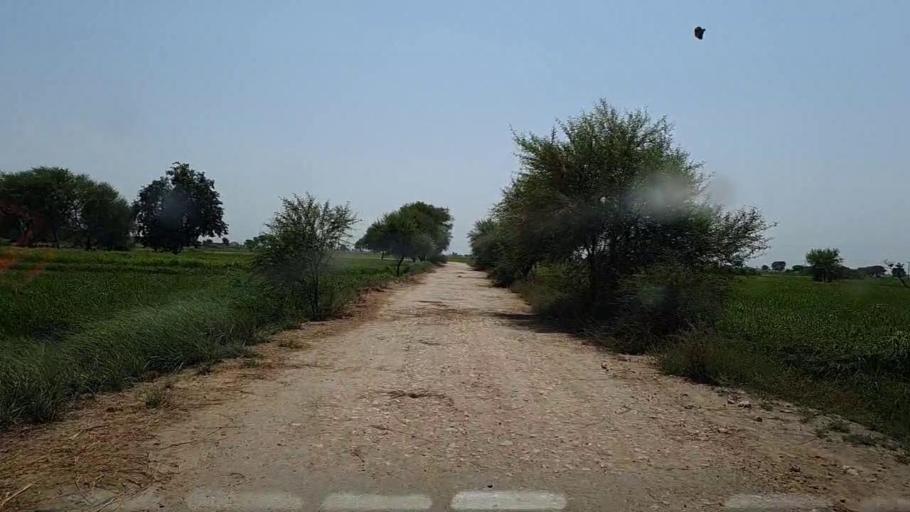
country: PK
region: Sindh
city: Kario
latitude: 24.6414
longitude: 68.4860
